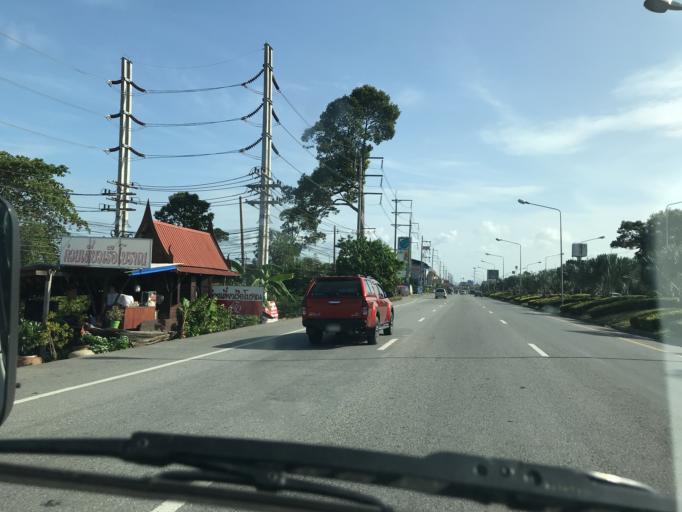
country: TH
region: Chon Buri
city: Bang Lamung
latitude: 13.0106
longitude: 100.9308
